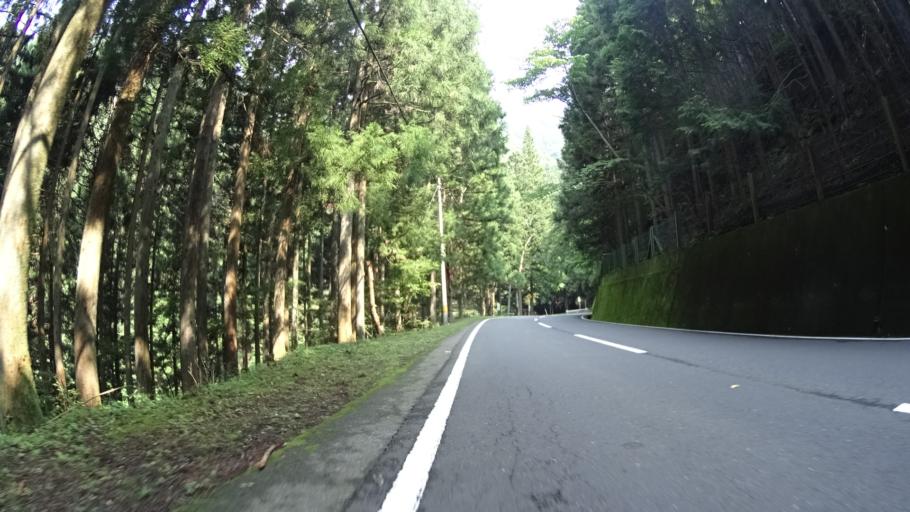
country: JP
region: Gunma
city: Tomioka
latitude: 36.0622
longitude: 138.8527
